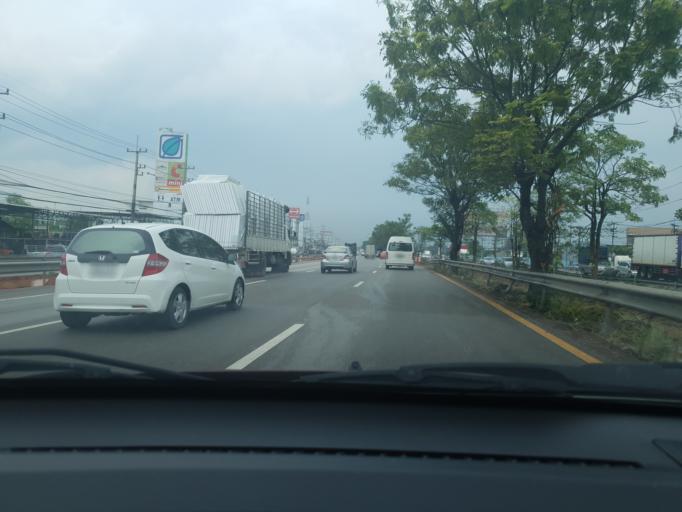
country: TH
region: Samut Sakhon
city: Samut Sakhon
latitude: 13.5926
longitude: 100.3377
